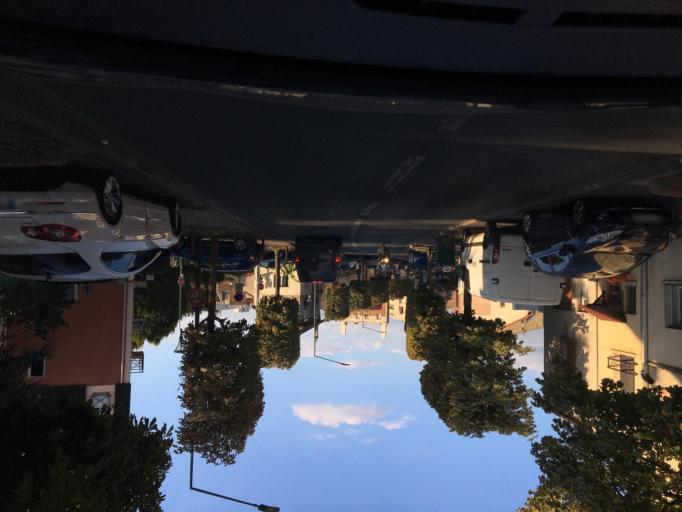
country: FR
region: Ile-de-France
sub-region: Departement du Val-de-Marne
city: Fontenay-sous-Bois
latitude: 48.8548
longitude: 2.4684
